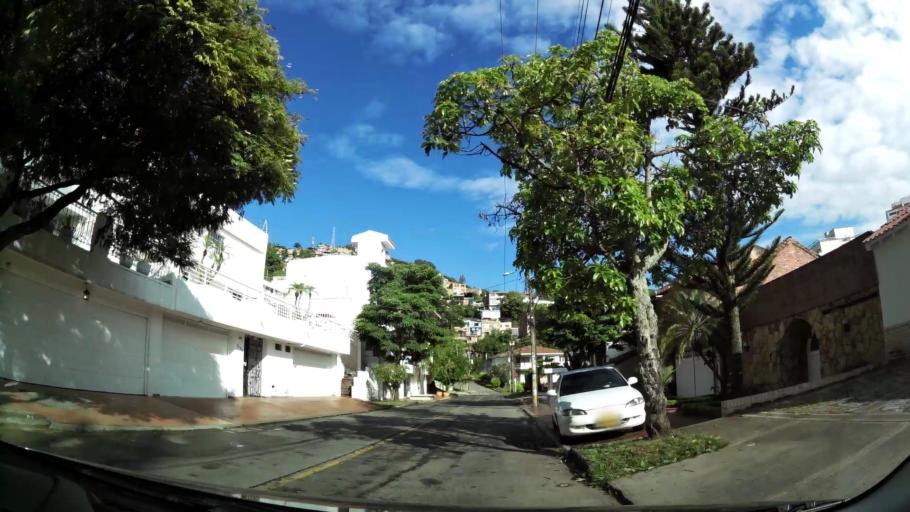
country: CO
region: Valle del Cauca
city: Cali
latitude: 3.4398
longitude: -76.5477
